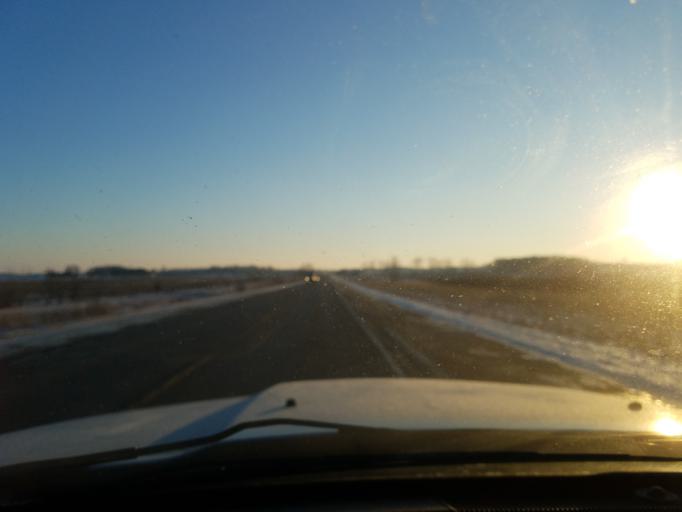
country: US
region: Indiana
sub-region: Marshall County
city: Bremen
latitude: 41.4606
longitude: -86.1890
